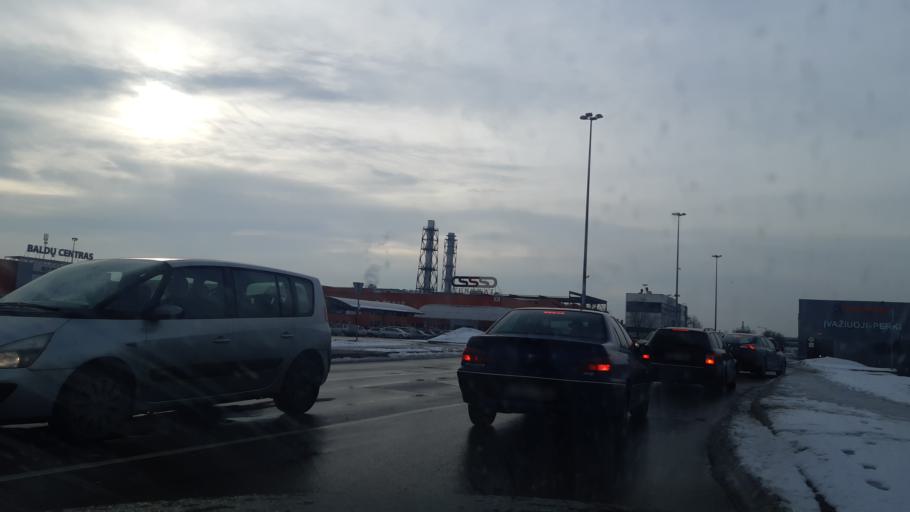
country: LT
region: Kauno apskritis
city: Dainava (Kaunas)
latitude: 54.9100
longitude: 23.9864
